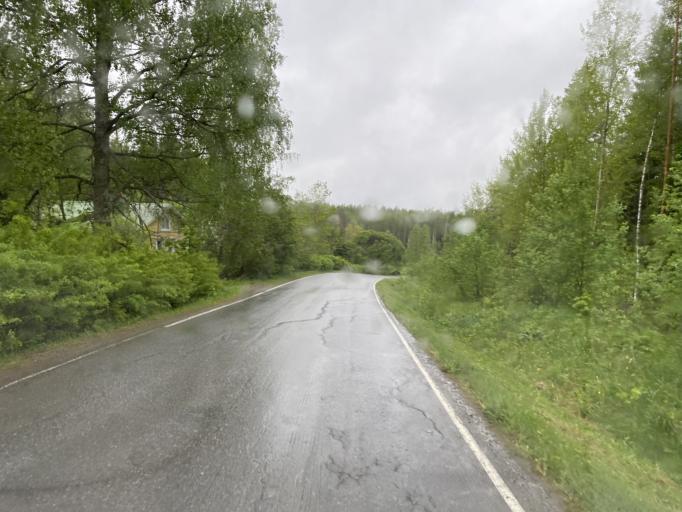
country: FI
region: Pirkanmaa
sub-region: Etelae-Pirkanmaa
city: Urjala
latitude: 60.9687
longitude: 23.5258
